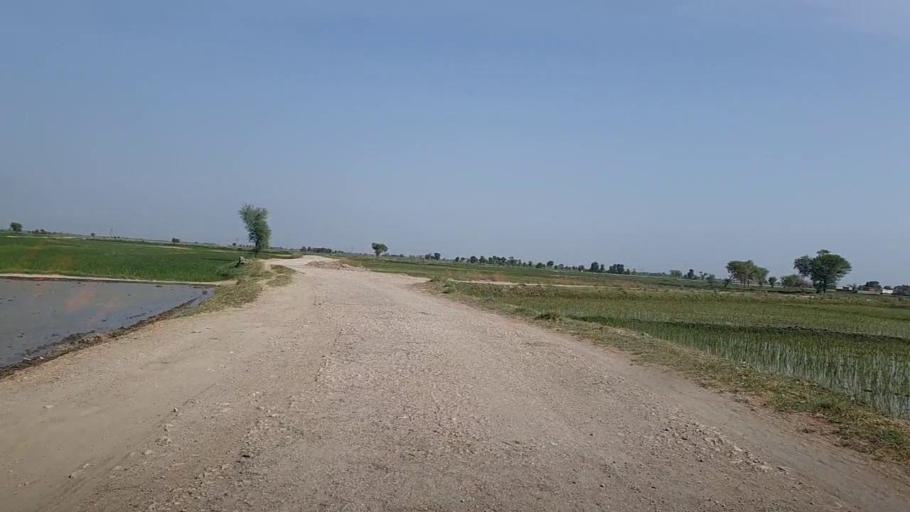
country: PK
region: Sindh
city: Mehar
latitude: 27.1134
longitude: 67.8453
